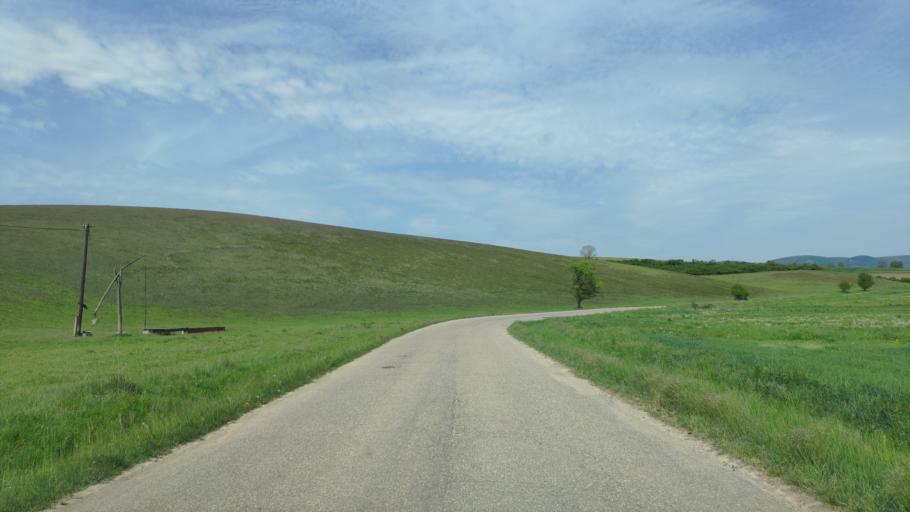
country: HU
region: Borsod-Abauj-Zemplen
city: Ozd
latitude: 48.4148
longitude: 20.2327
